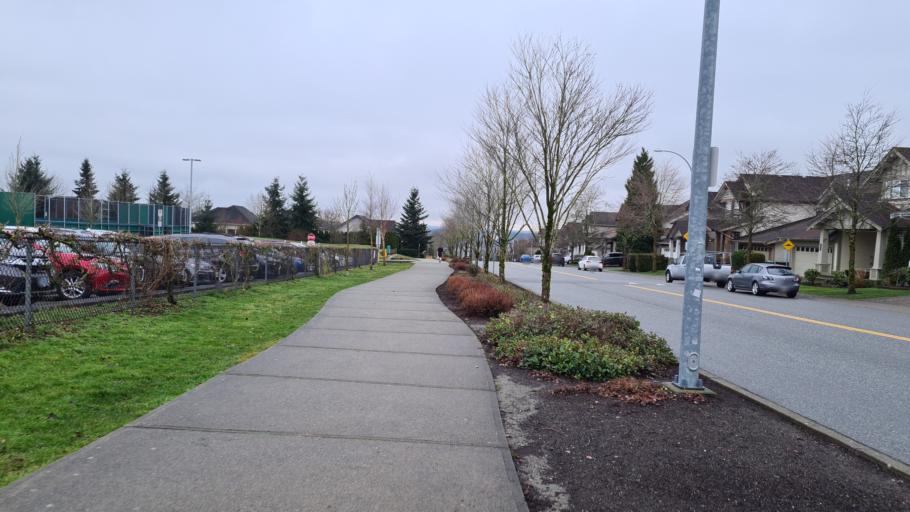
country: CA
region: British Columbia
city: Langley
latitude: 49.1317
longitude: -122.6645
